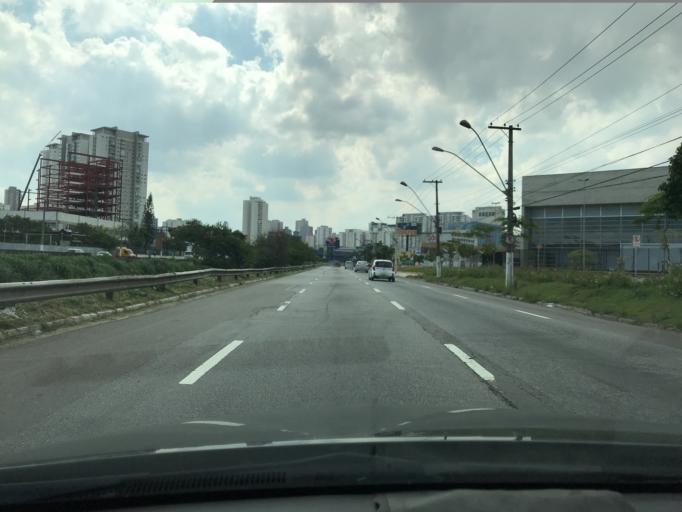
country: BR
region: Sao Paulo
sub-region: Santo Andre
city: Santo Andre
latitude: -23.6456
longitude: -46.5286
